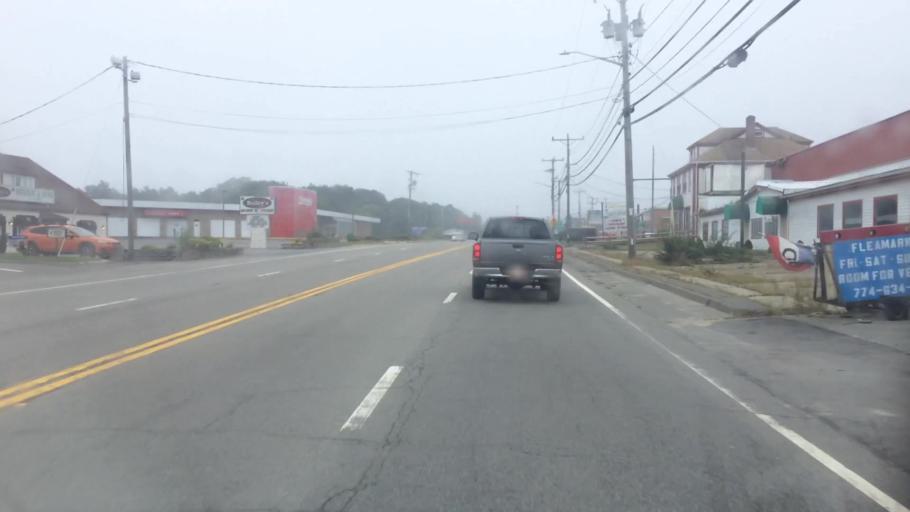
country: US
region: Massachusetts
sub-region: Plymouth County
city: Onset
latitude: 41.7573
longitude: -70.6569
